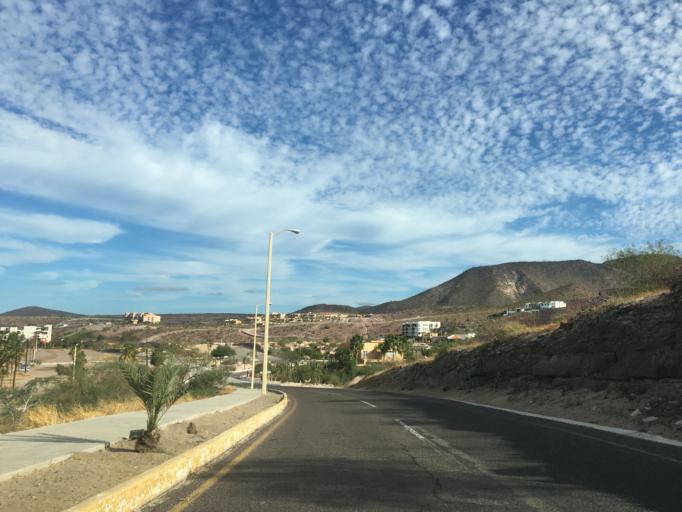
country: MX
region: Baja California Sur
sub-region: La Paz
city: La Paz
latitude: 24.2014
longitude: -110.2985
